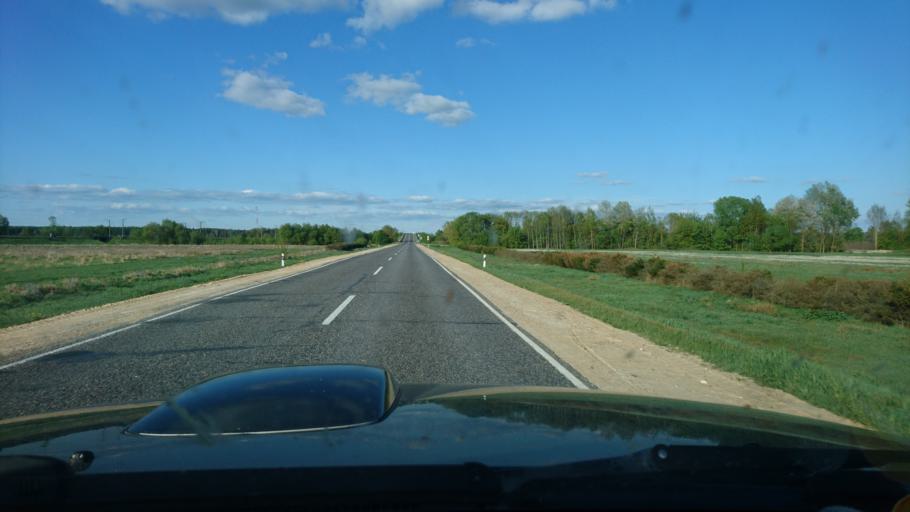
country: BY
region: Brest
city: Nyakhachava
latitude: 52.6352
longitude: 25.1879
